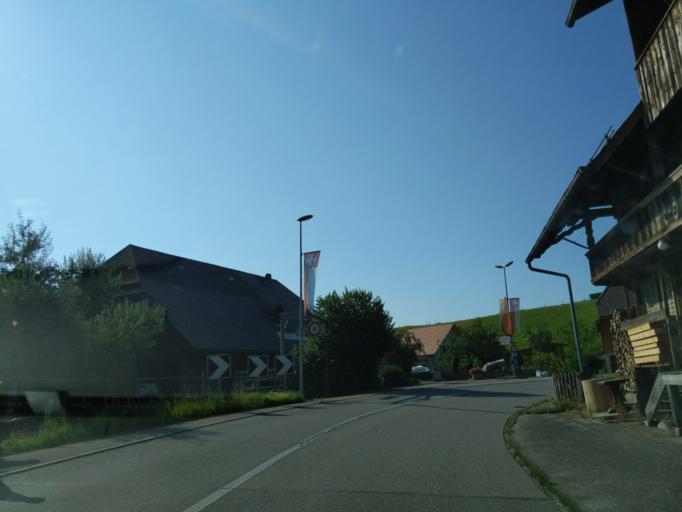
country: CH
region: Bern
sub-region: Emmental District
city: Lauperswil
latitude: 46.9675
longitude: 7.7422
